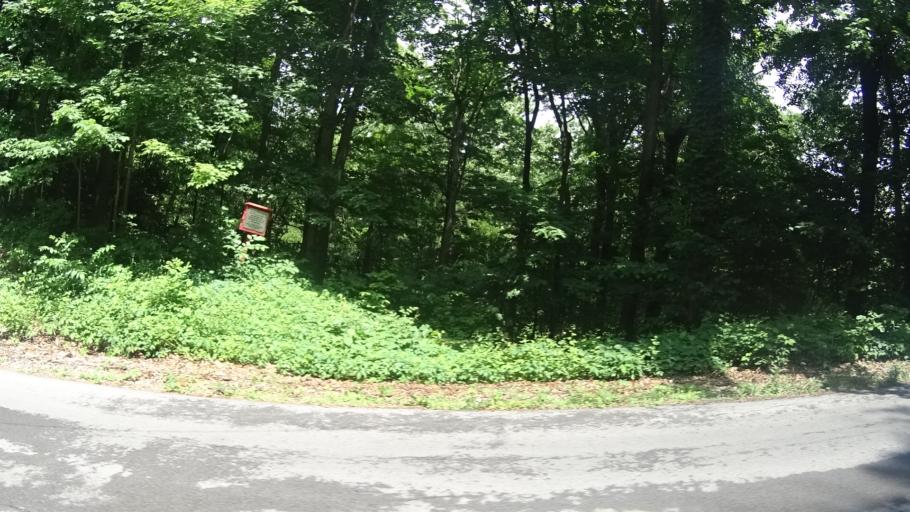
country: US
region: Ohio
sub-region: Erie County
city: Milan
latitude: 41.2920
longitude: -82.5941
